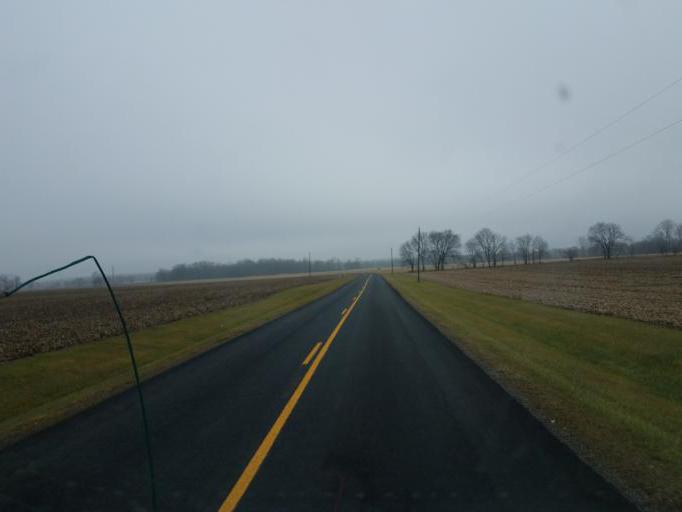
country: US
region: Ohio
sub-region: Champaign County
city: North Lewisburg
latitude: 40.2332
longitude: -83.5444
